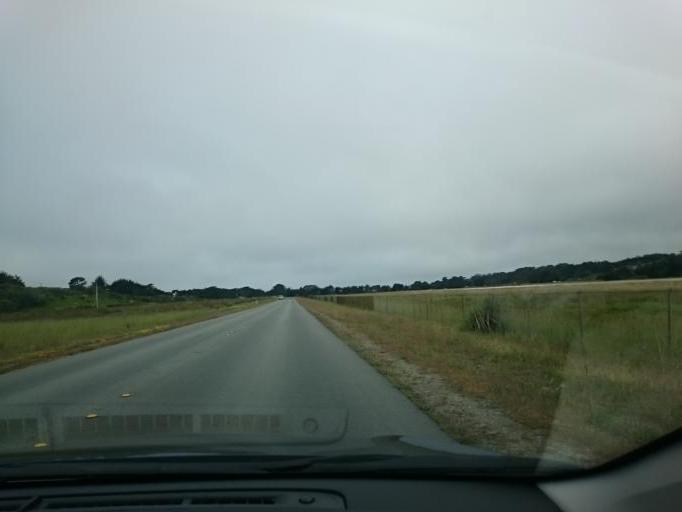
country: US
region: California
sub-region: San Mateo County
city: Moss Beach
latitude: 37.5145
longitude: -122.5039
